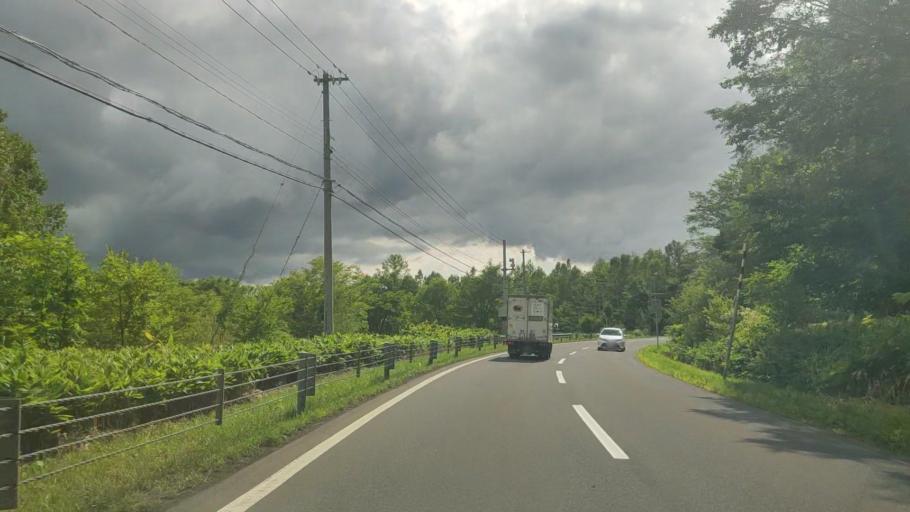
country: JP
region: Hokkaido
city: Date
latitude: 42.6545
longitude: 141.0680
